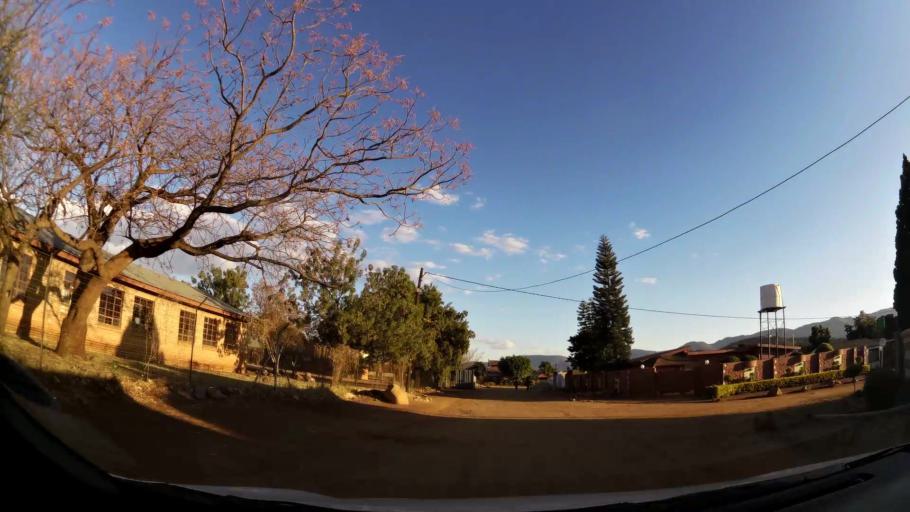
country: ZA
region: Limpopo
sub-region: Waterberg District Municipality
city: Mokopane
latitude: -24.1459
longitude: 28.9857
